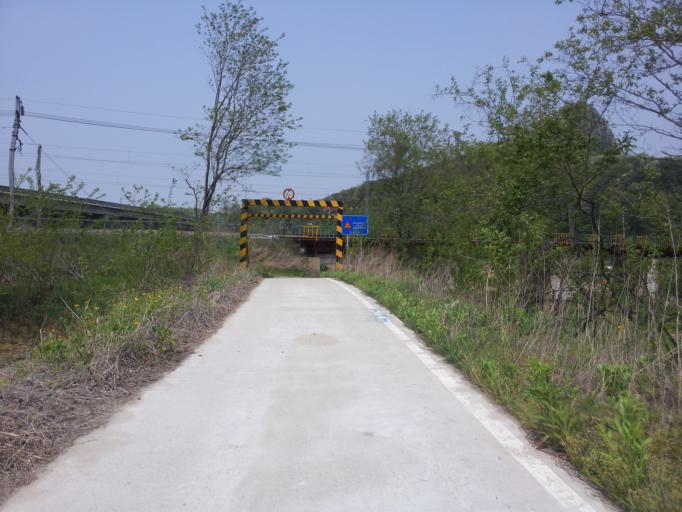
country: KR
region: Daejeon
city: Daejeon
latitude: 36.2635
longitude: 127.2908
